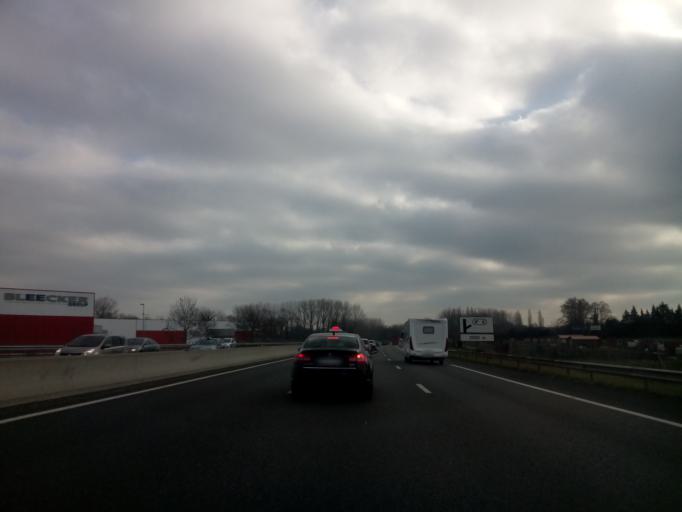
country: FR
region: Rhone-Alpes
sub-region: Departement de l'Isere
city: La Verpilliere
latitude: 45.6437
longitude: 5.1409
